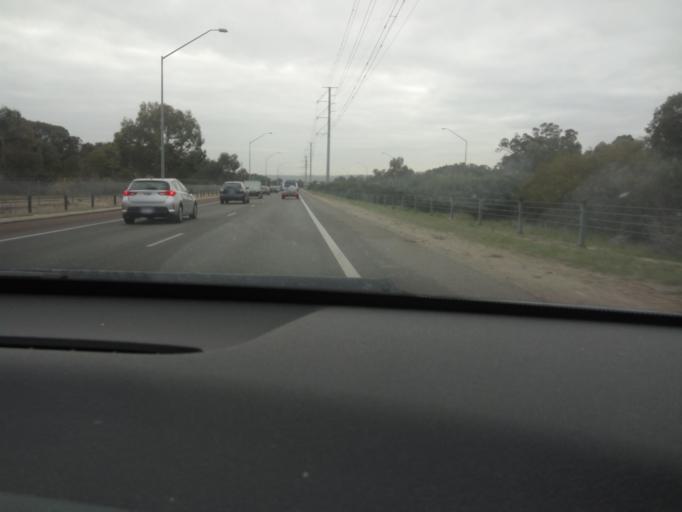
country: AU
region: Western Australia
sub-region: Gosnells
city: Langford
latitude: -32.0418
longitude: 115.9522
